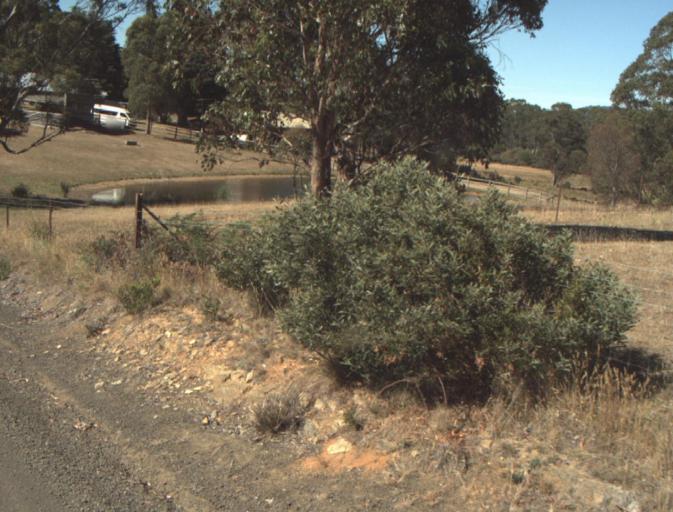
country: AU
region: Tasmania
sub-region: Launceston
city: Newstead
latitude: -41.3059
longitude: 147.3177
